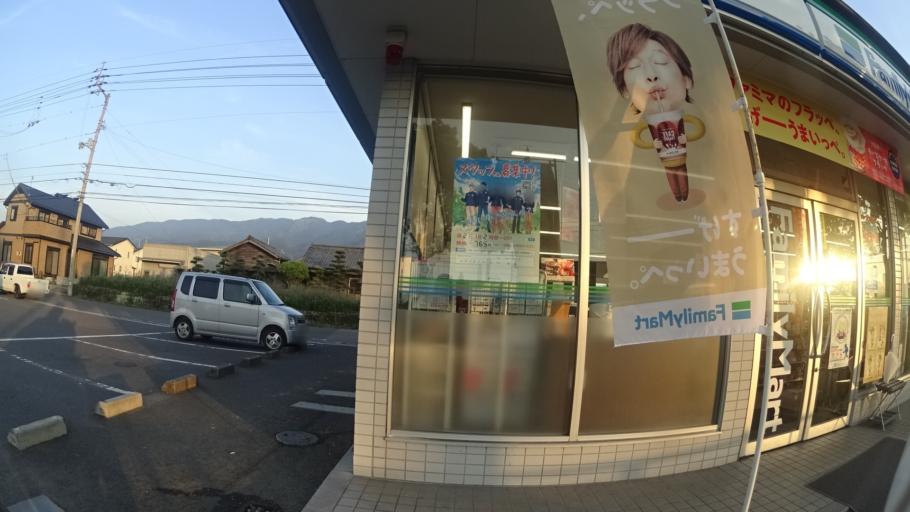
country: JP
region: Ehime
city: Kawanoecho
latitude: 33.9846
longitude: 133.5584
